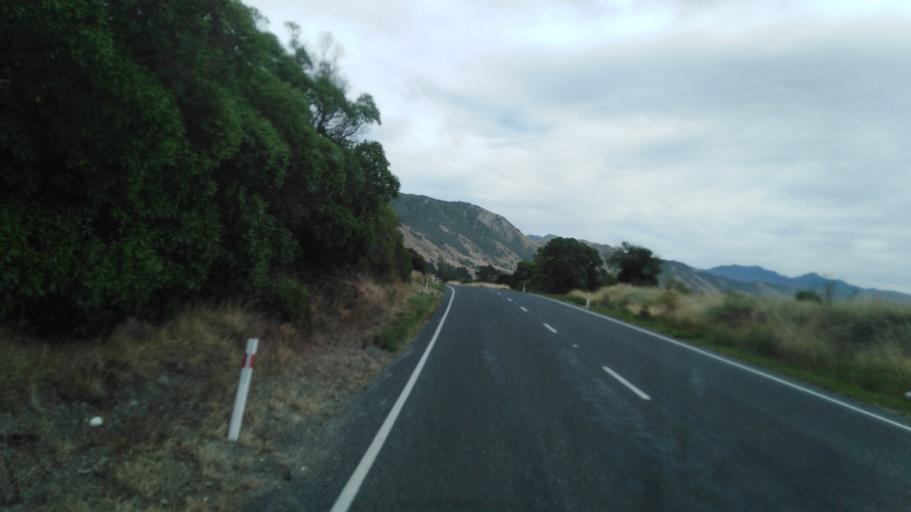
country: NZ
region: Canterbury
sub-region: Kaikoura District
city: Kaikoura
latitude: -42.1442
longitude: 173.9268
